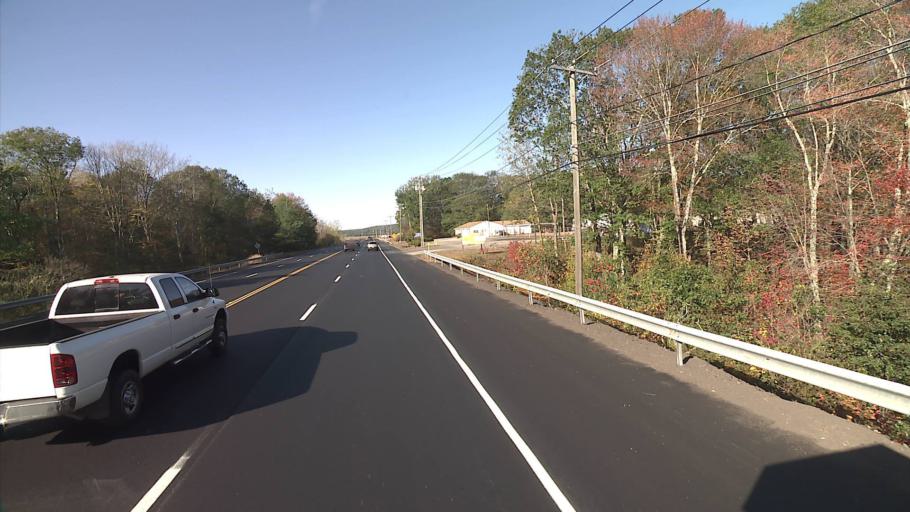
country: US
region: Connecticut
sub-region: Windham County
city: Windham
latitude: 41.7479
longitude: -72.1589
